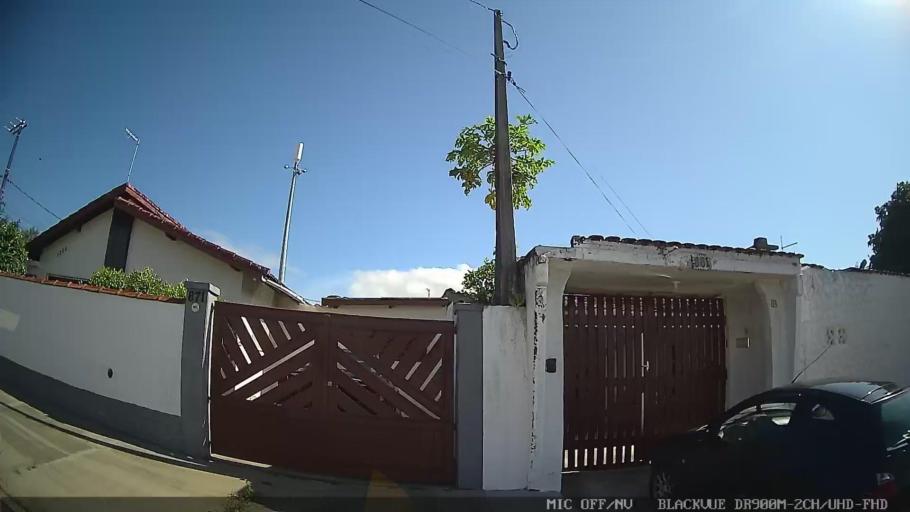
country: BR
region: Sao Paulo
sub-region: Peruibe
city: Peruibe
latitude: -24.3072
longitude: -46.9892
